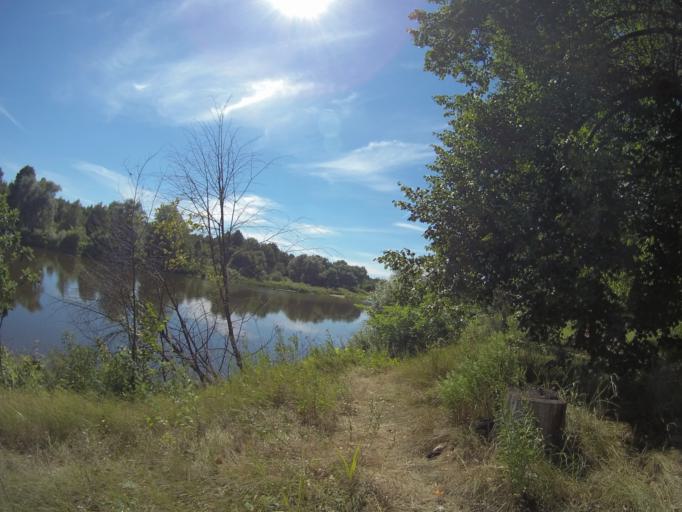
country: RU
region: Vladimir
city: Raduzhnyy
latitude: 56.0484
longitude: 40.3534
